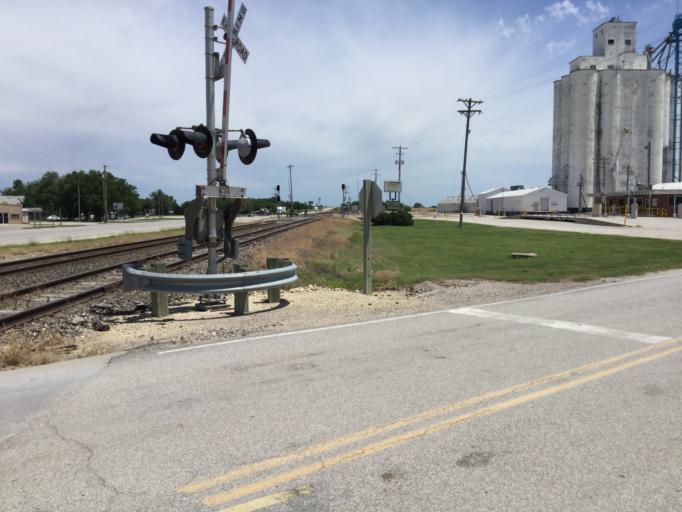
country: US
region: Kansas
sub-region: Harvey County
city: North Newton
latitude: 38.1168
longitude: -97.2563
